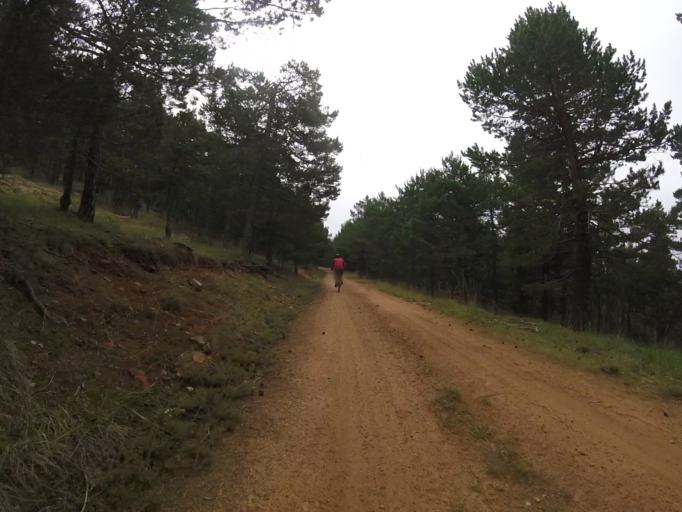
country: ES
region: Aragon
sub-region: Provincia de Teruel
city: Valdelinares
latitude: 40.3612
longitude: -0.6100
